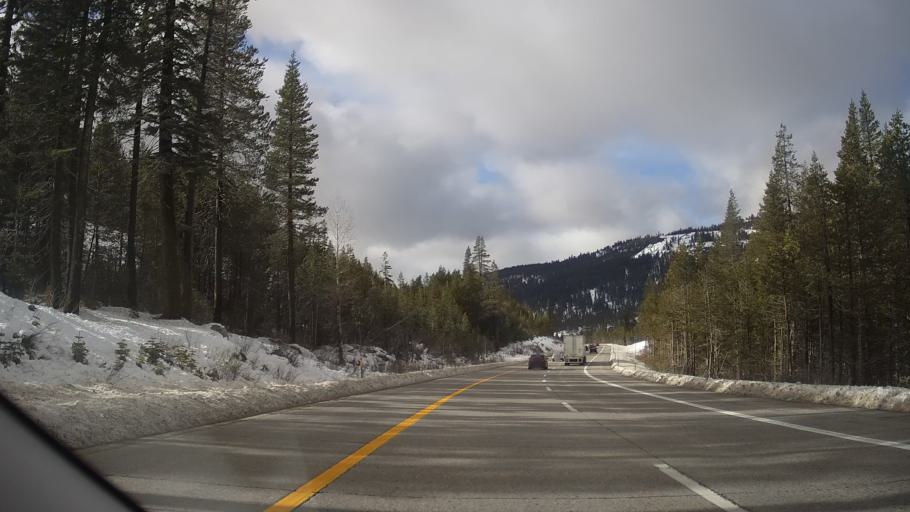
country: US
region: California
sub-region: Nevada County
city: Truckee
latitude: 39.3228
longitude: -120.4076
